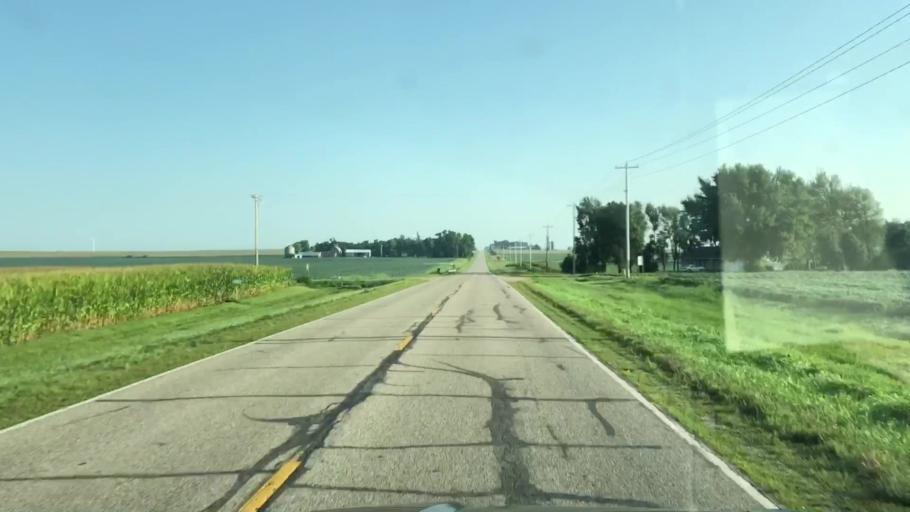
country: US
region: Iowa
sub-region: Lyon County
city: George
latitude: 43.3594
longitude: -95.9983
